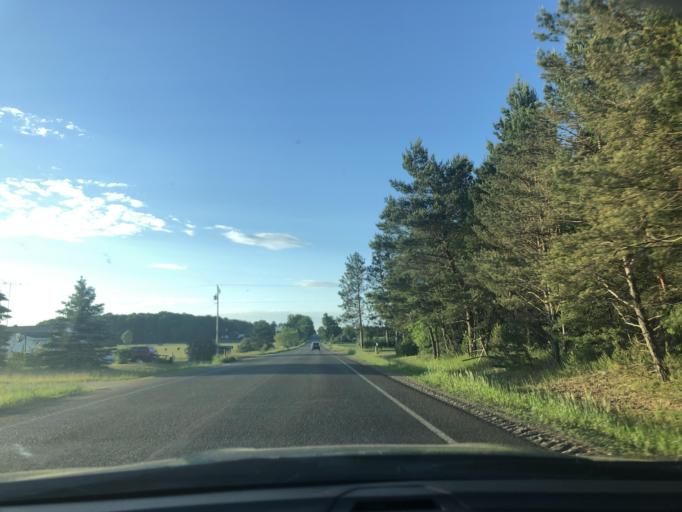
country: US
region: Michigan
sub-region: Missaukee County
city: Lake City
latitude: 44.3939
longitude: -85.0757
